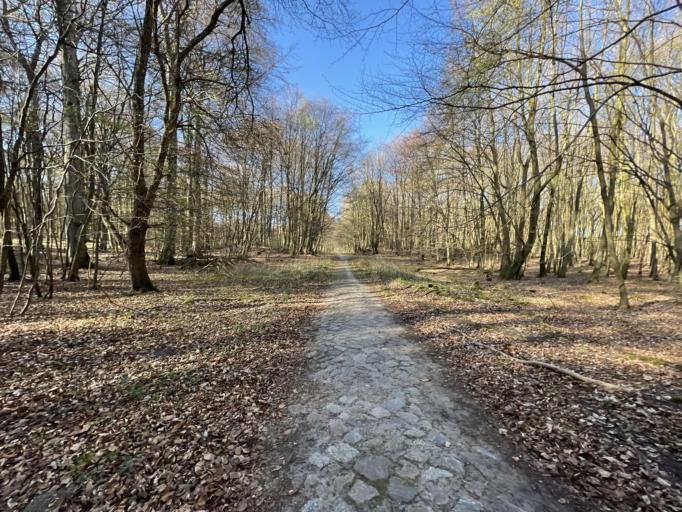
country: DE
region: Mecklenburg-Vorpommern
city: Sassnitz
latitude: 54.5310
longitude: 13.6428
